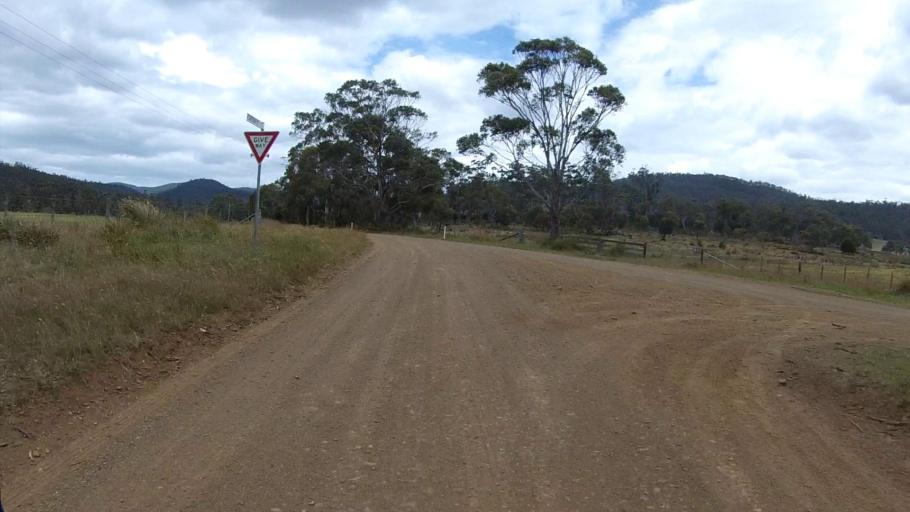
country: AU
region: Tasmania
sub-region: Sorell
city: Sorell
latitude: -42.6440
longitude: 147.9006
